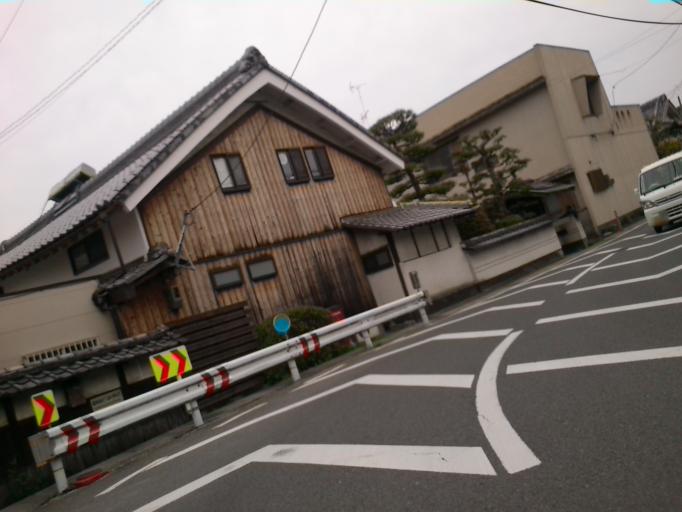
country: JP
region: Kyoto
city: Tanabe
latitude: 34.8368
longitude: 135.7507
